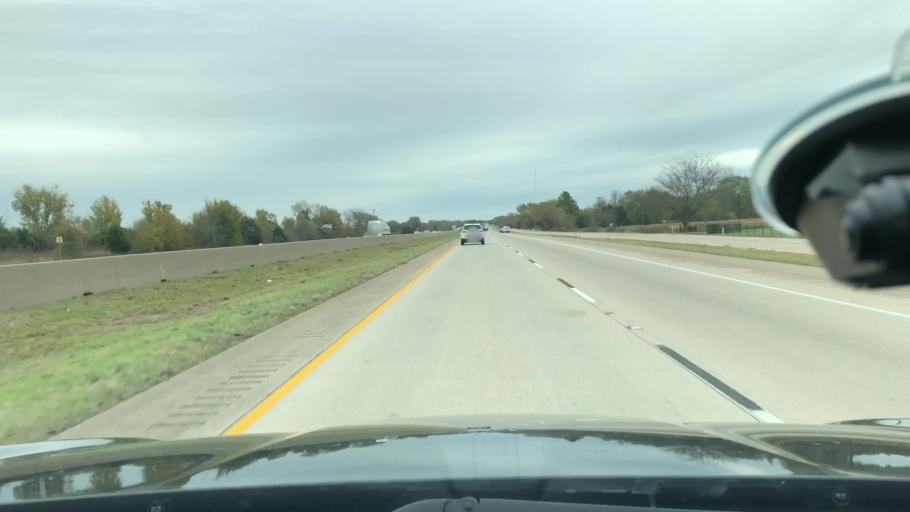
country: US
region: Texas
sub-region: Hopkins County
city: Sulphur Springs
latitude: 33.1288
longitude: -95.7636
